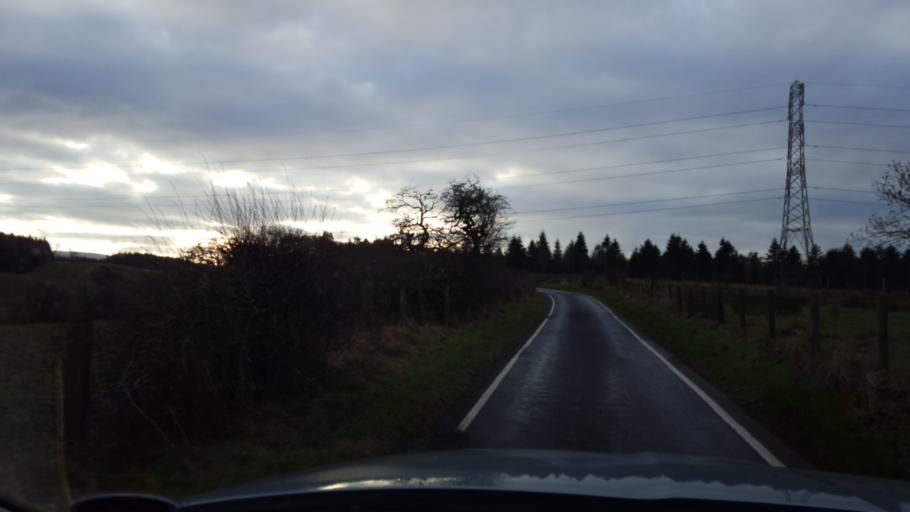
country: GB
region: Scotland
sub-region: West Lothian
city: Mid Calder
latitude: 55.8440
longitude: -3.5031
